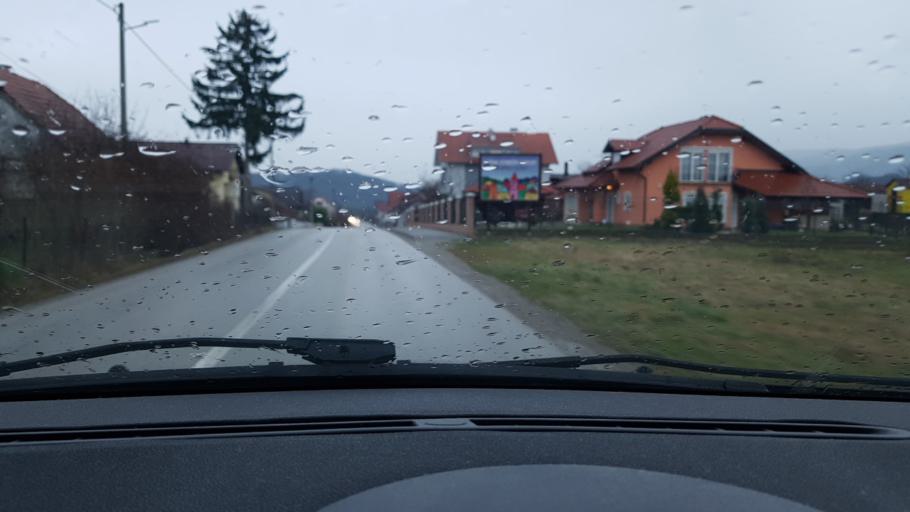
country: HR
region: Krapinsko-Zagorska
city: Oroslavje
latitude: 45.9779
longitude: 15.9142
